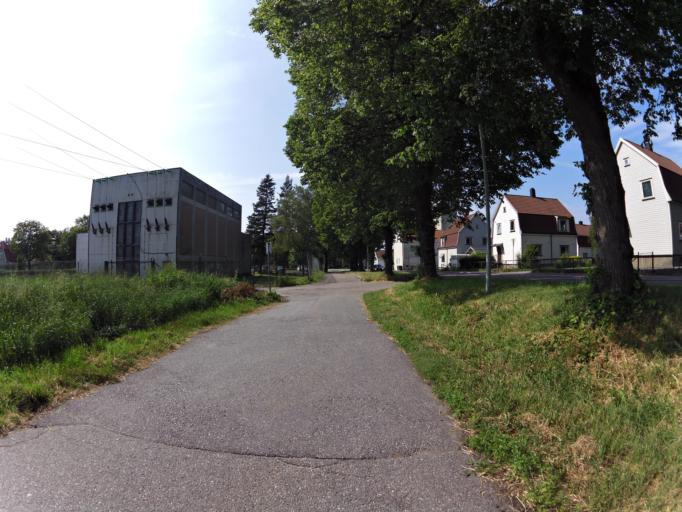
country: NO
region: Ostfold
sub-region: Sarpsborg
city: Sarpsborg
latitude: 59.2732
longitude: 11.1025
